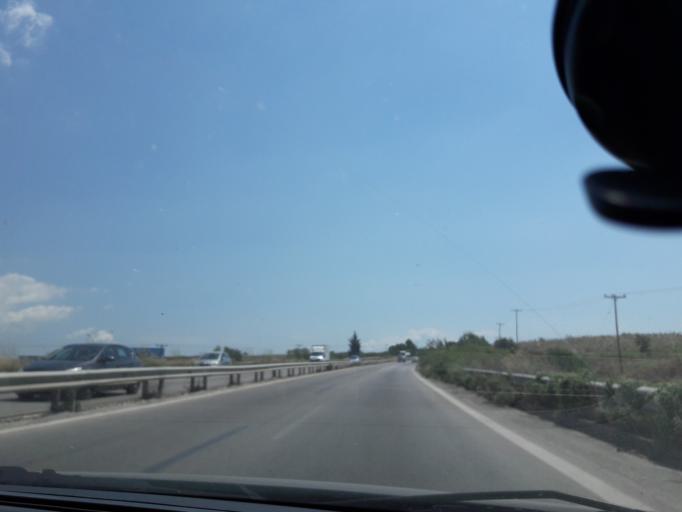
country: GR
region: Central Macedonia
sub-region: Nomos Chalkidikis
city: Nea Kallikrateia
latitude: 40.3051
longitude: 23.1303
